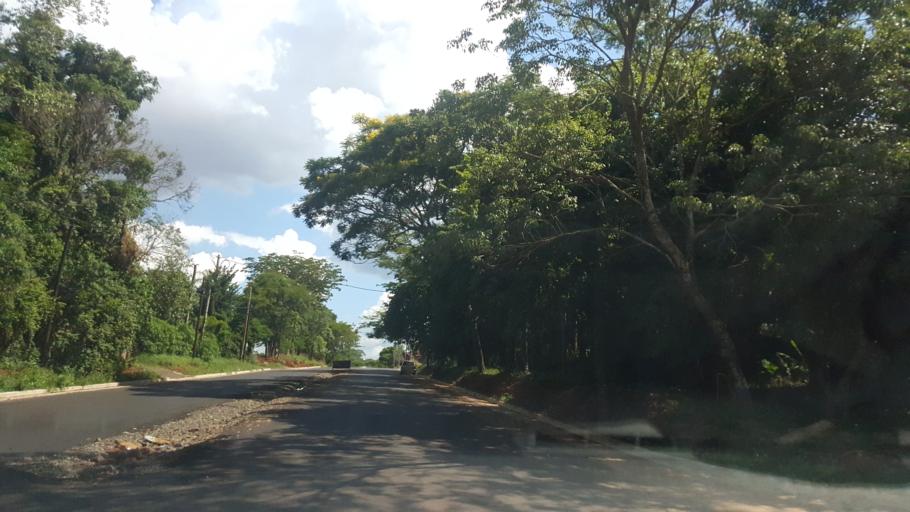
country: AR
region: Misiones
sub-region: Departamento de Capital
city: Posadas
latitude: -27.3607
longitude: -55.9232
